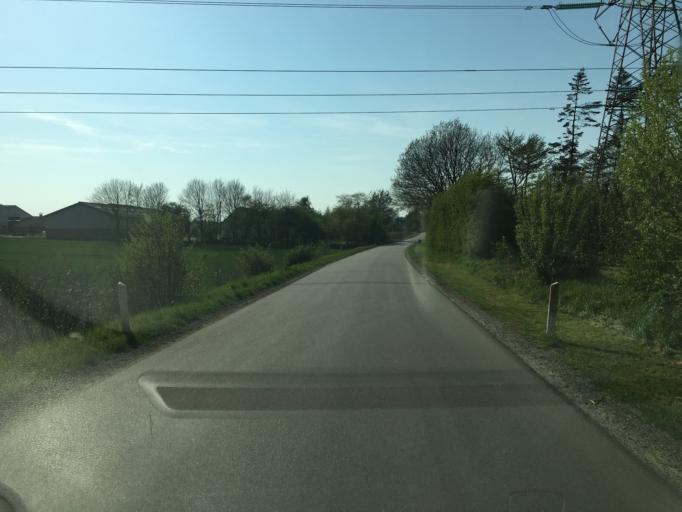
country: DK
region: South Denmark
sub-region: Haderslev Kommune
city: Vojens
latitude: 55.2321
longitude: 9.3393
